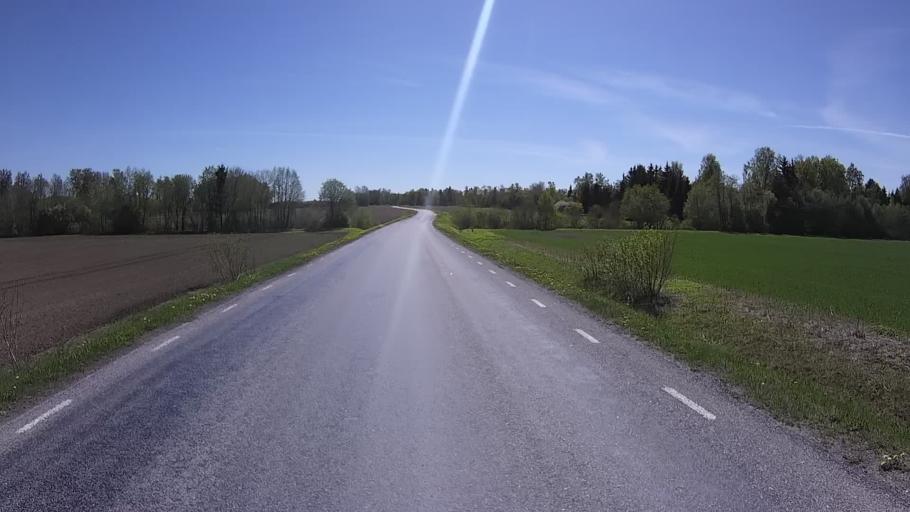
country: EE
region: Harju
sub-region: Raasiku vald
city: Raasiku
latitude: 59.0957
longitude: 25.1716
